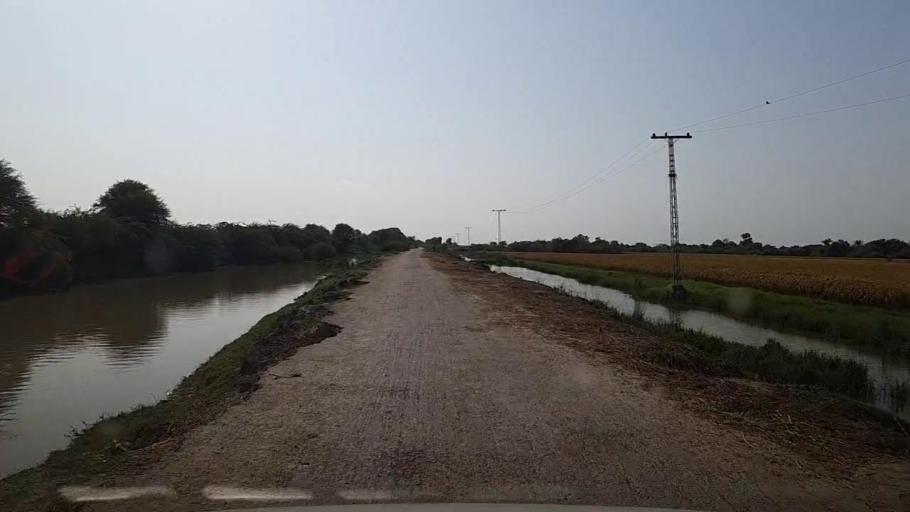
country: PK
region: Sindh
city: Kario
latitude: 24.8064
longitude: 68.5334
